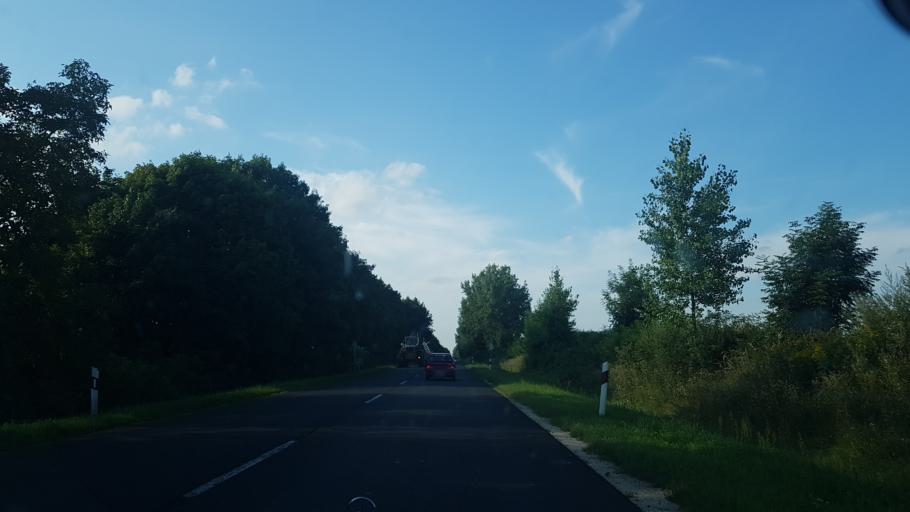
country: HU
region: Somogy
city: Segesd
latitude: 46.3113
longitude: 17.3488
